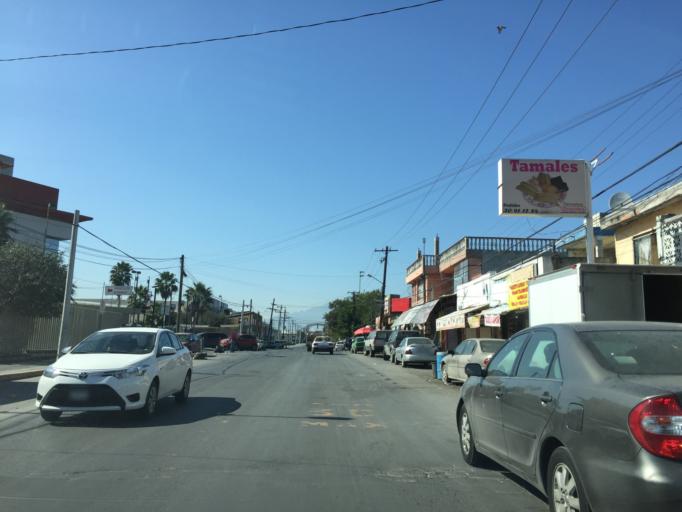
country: MX
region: Nuevo Leon
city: Guadalupe
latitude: 25.6952
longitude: -100.2227
